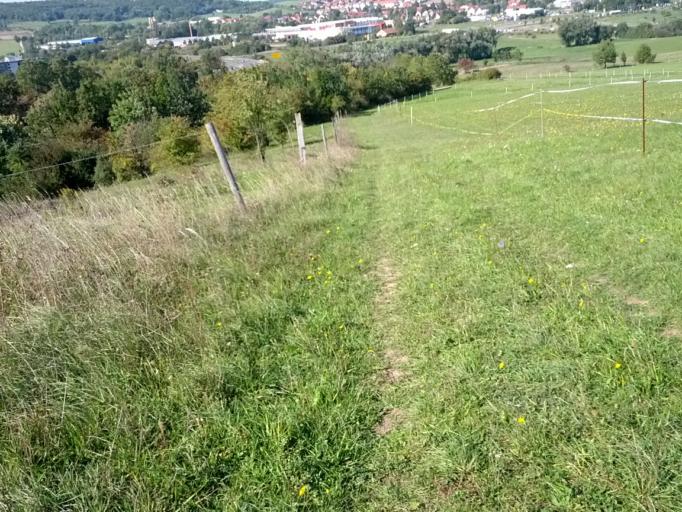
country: DE
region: Thuringia
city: Eisenach
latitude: 50.9938
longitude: 10.3224
